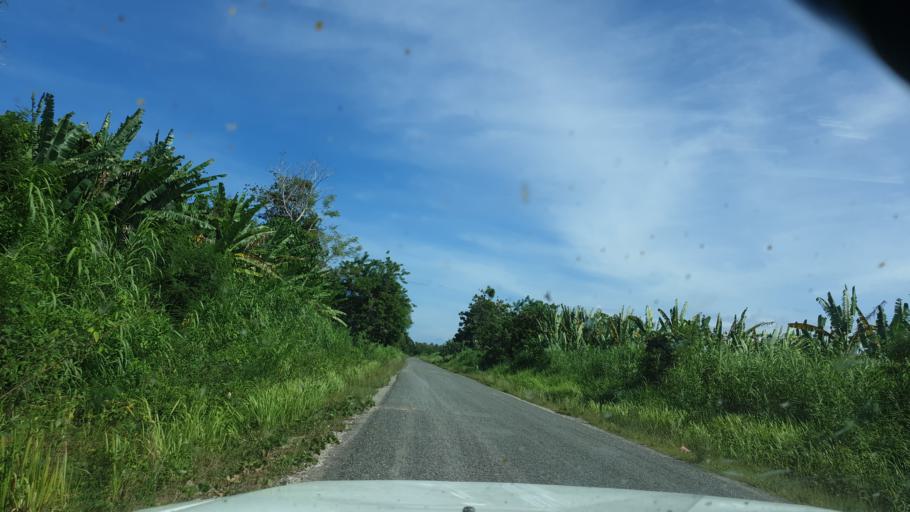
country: PG
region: Madang
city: Madang
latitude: -4.6959
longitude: 145.6124
